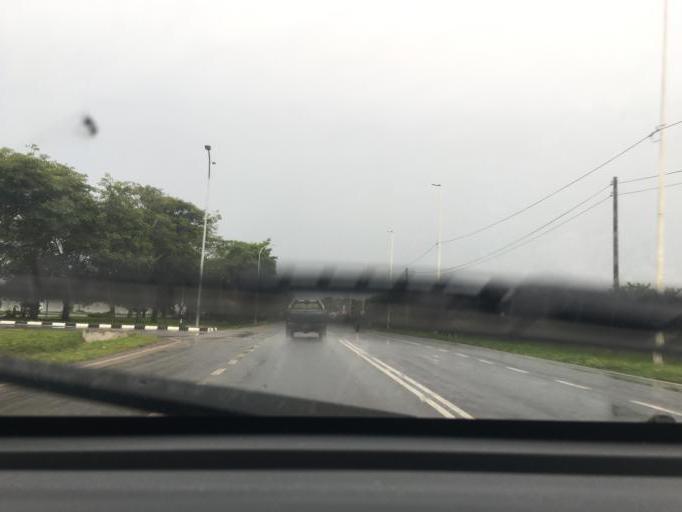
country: MY
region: Kedah
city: Sungai Petani
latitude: 5.5950
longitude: 100.6395
